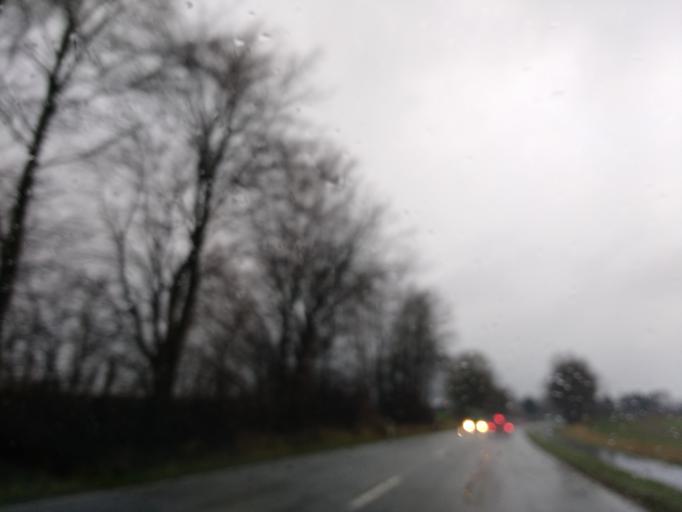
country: DE
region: Schleswig-Holstein
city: Holzbunge
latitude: 54.3721
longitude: 9.7024
